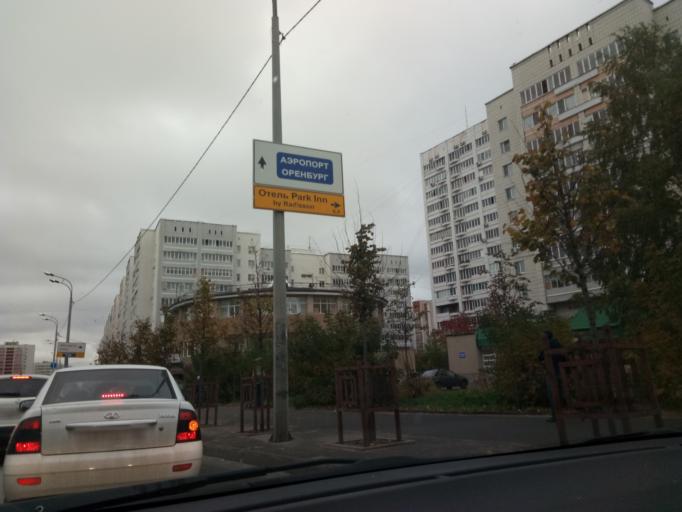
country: RU
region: Tatarstan
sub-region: Gorod Kazan'
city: Kazan
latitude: 55.7874
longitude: 49.1513
